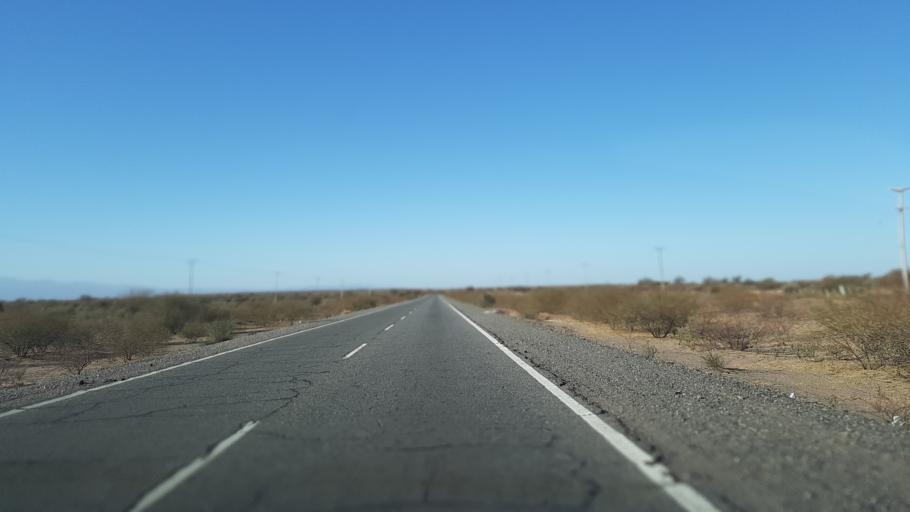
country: AR
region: San Juan
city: Caucete
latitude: -31.6003
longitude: -67.7004
